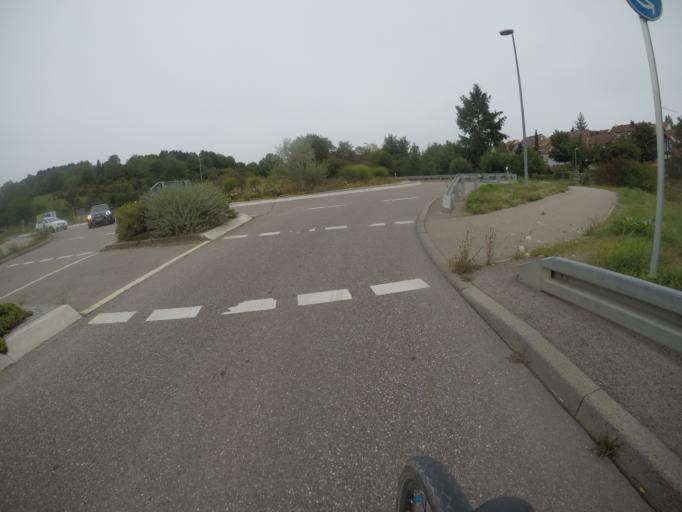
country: DE
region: Baden-Wuerttemberg
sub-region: Karlsruhe Region
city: Heimsheim
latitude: 48.8106
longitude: 8.8608
